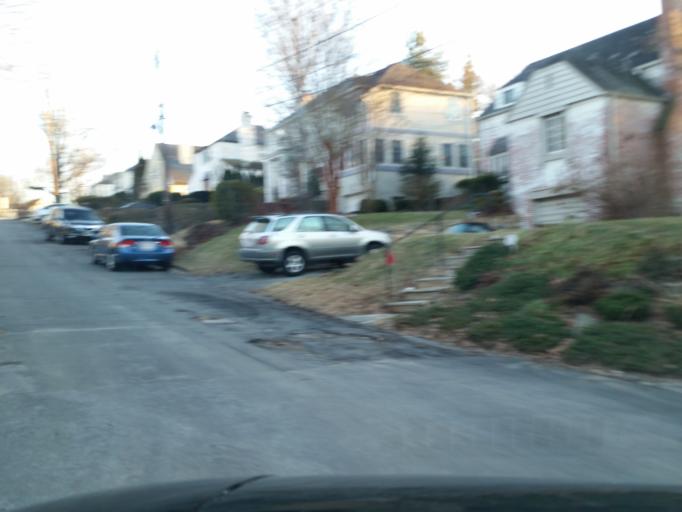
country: US
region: Maryland
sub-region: Montgomery County
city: Friendship Village
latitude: 38.9569
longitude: -77.0953
